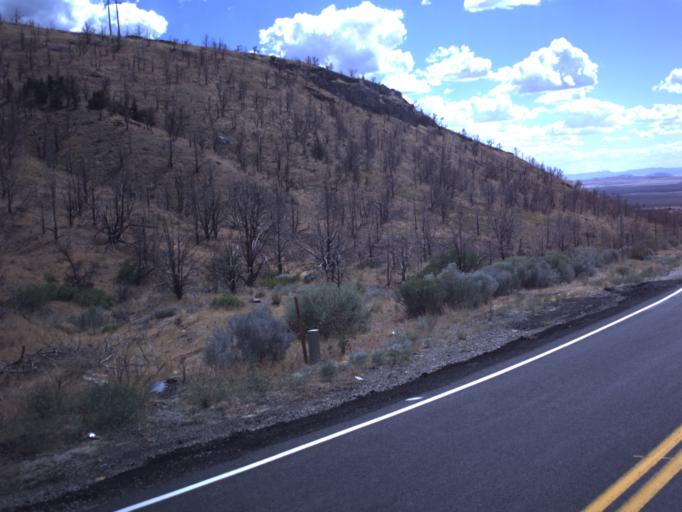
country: US
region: Utah
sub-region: Tooele County
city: Grantsville
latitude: 40.3437
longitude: -112.6041
